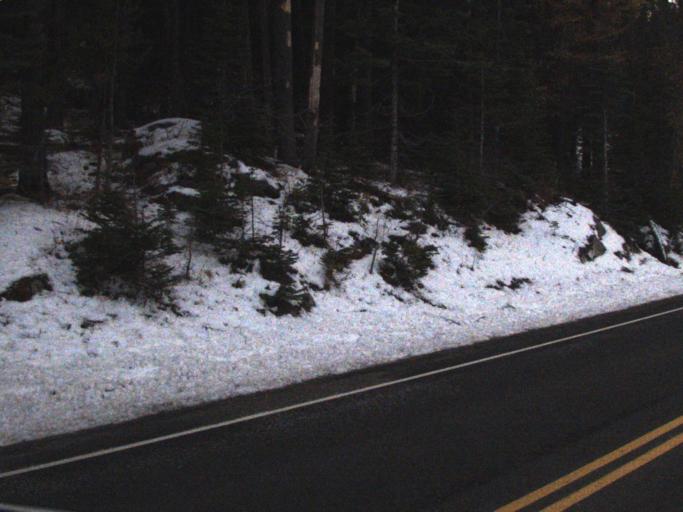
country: US
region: Washington
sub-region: Ferry County
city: Republic
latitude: 48.6049
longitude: -118.4687
